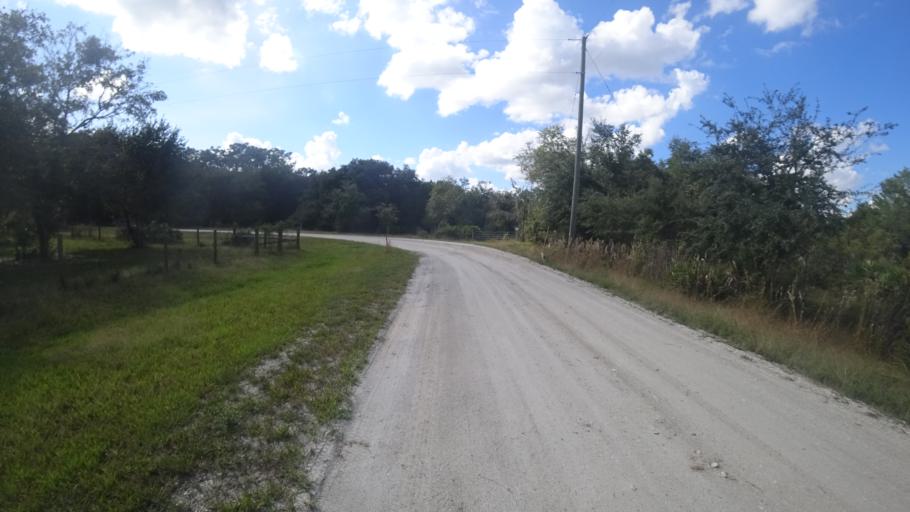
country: US
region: Florida
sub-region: Hillsborough County
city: Wimauma
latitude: 27.4374
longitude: -82.1501
